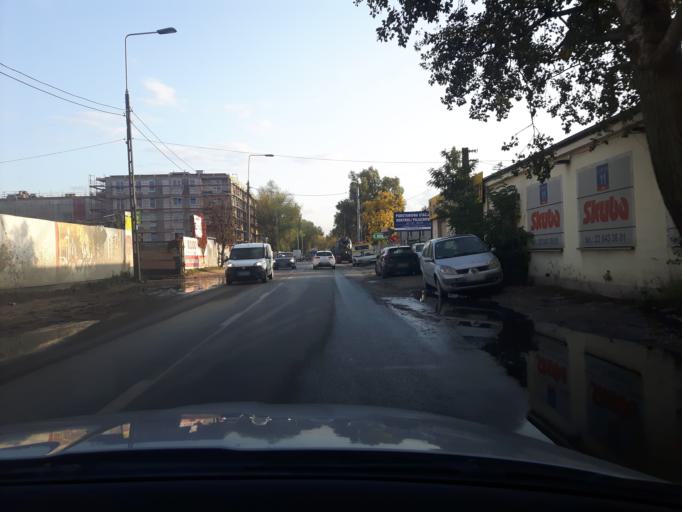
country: PL
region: Masovian Voivodeship
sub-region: Warszawa
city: Wlochy
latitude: 52.1615
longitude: 20.9923
